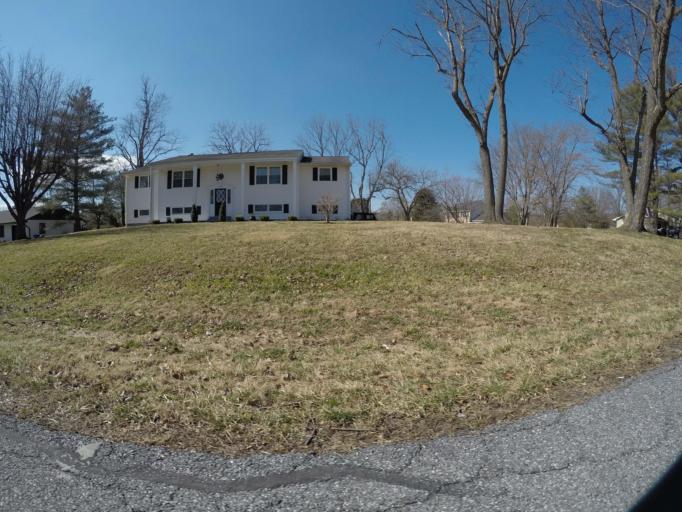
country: US
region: Maryland
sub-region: Howard County
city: Columbia
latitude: 39.2841
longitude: -76.8429
